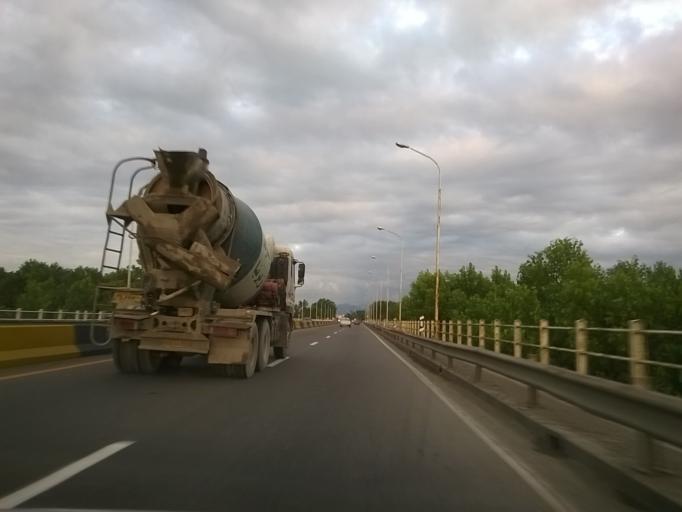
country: IR
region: Gilan
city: Astaneh-ye Ashrafiyeh
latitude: 37.2627
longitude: 49.9243
